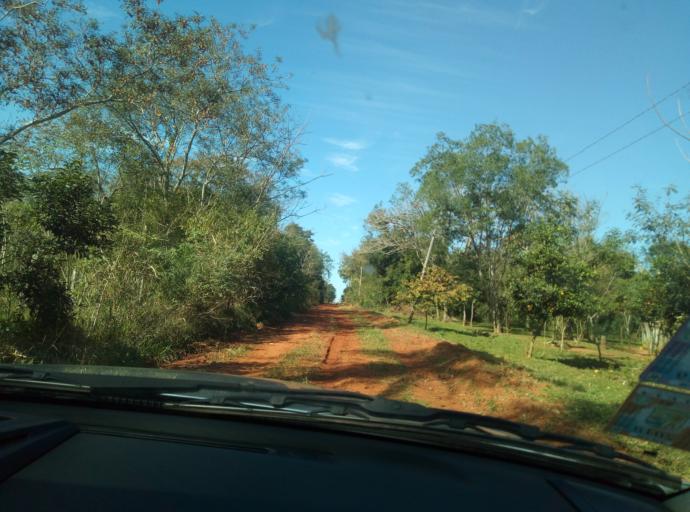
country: PY
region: Caaguazu
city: Carayao
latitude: -25.1704
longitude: -56.2984
